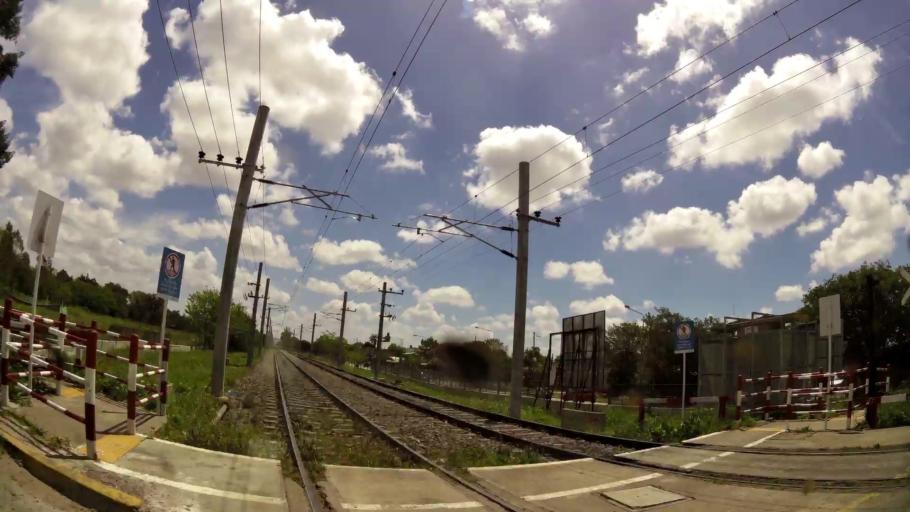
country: AR
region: Buenos Aires
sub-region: Partido de Quilmes
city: Quilmes
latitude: -34.8173
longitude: -58.2372
